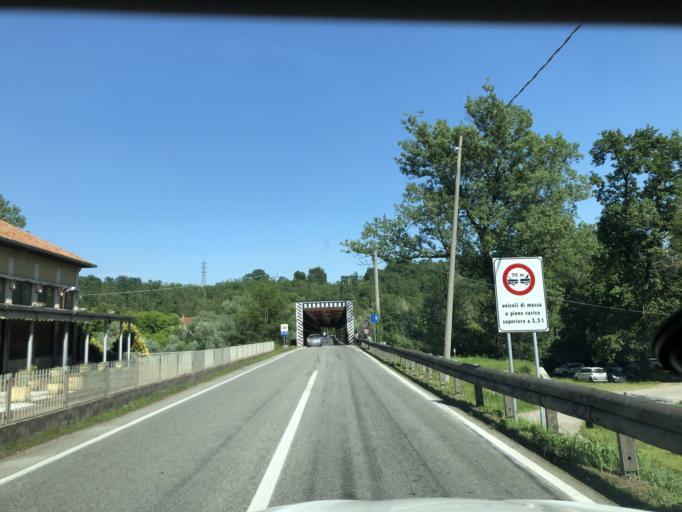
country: IT
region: Lombardy
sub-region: Provincia di Varese
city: Vizzola Ticino
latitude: 45.5896
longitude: 8.7023
